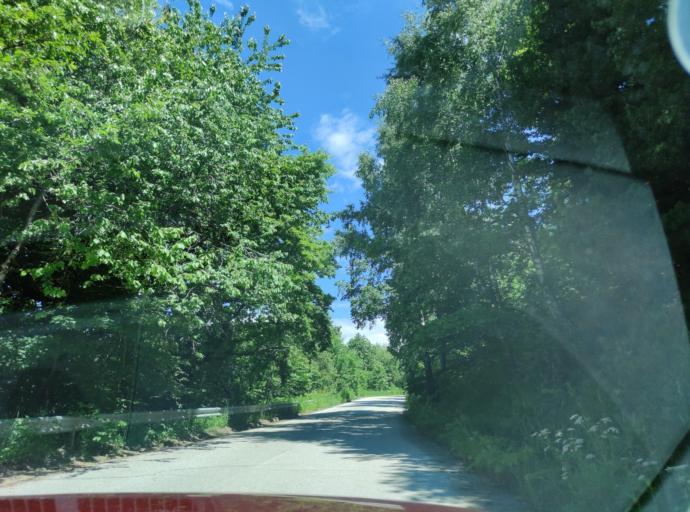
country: BG
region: Sofia-Capital
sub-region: Stolichna Obshtina
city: Sofia
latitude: 42.6344
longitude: 23.2308
